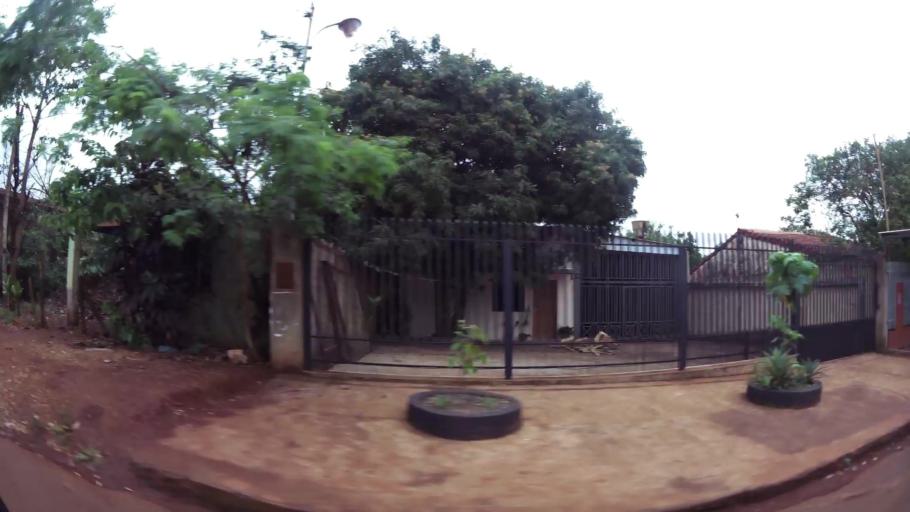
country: PY
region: Alto Parana
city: Presidente Franco
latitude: -25.5091
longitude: -54.6886
